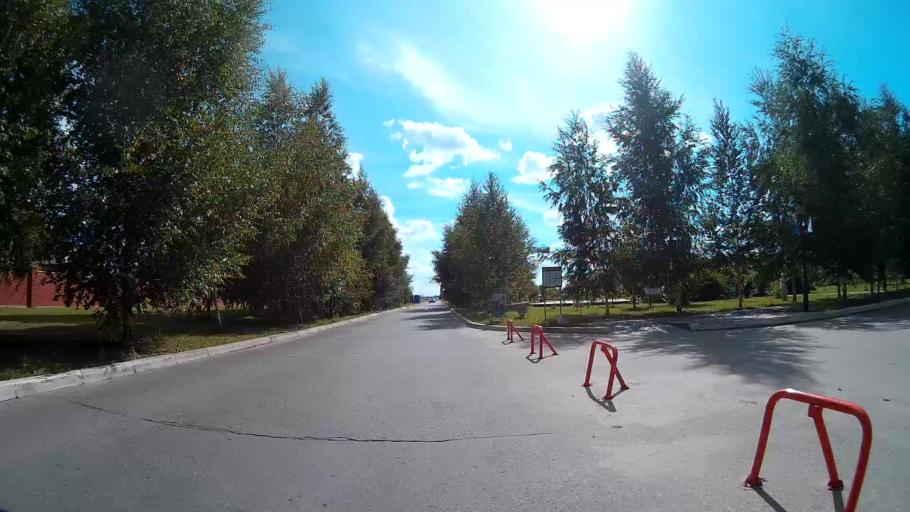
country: RU
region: Ulyanovsk
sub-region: Ulyanovskiy Rayon
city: Ulyanovsk
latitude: 54.2743
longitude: 48.2684
